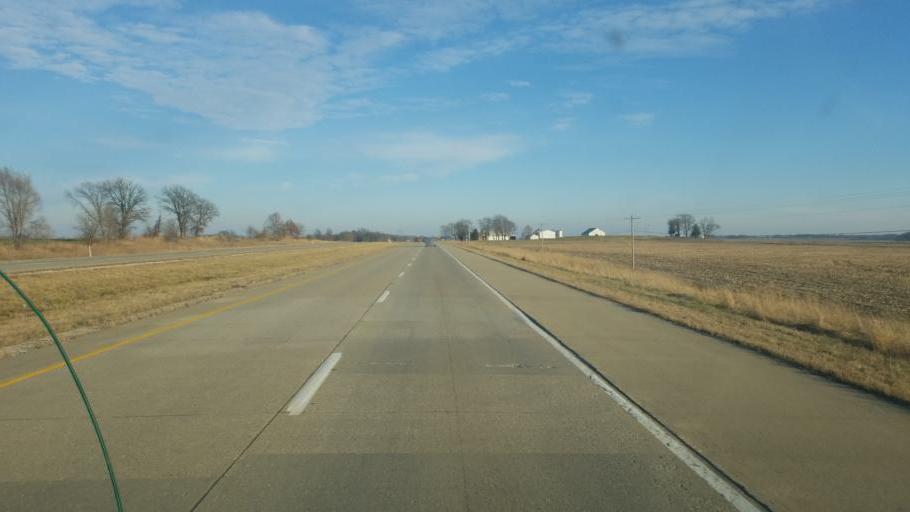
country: US
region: Indiana
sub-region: Knox County
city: Bicknell
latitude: 38.6741
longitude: -87.3642
